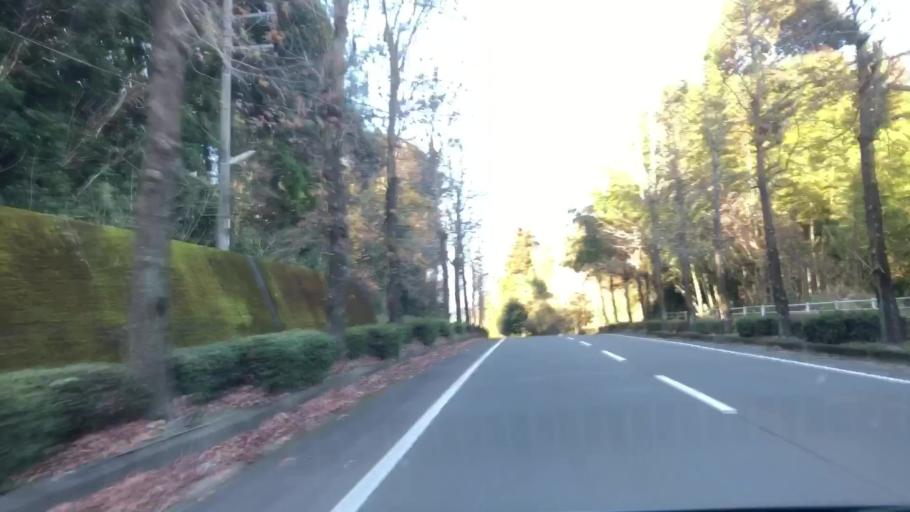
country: JP
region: Kagoshima
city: Satsumasendai
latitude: 31.8292
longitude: 130.4349
